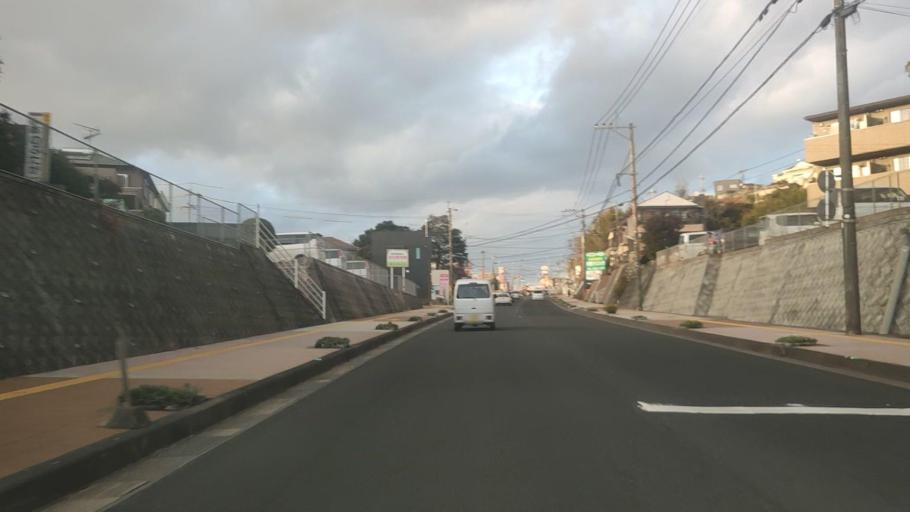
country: JP
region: Kagoshima
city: Kagoshima-shi
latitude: 31.6185
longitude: 130.5539
